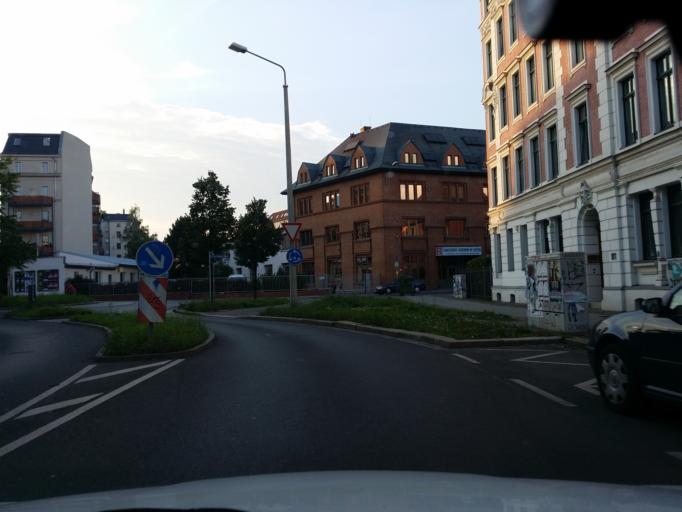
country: DE
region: Saxony
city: Leipzig
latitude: 51.3271
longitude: 12.3388
